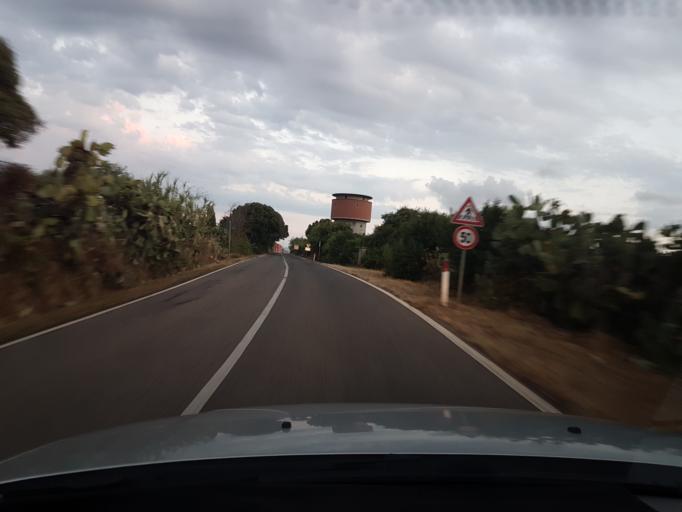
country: IT
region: Sardinia
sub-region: Provincia di Oristano
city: Tramatza
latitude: 40.0081
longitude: 8.6466
